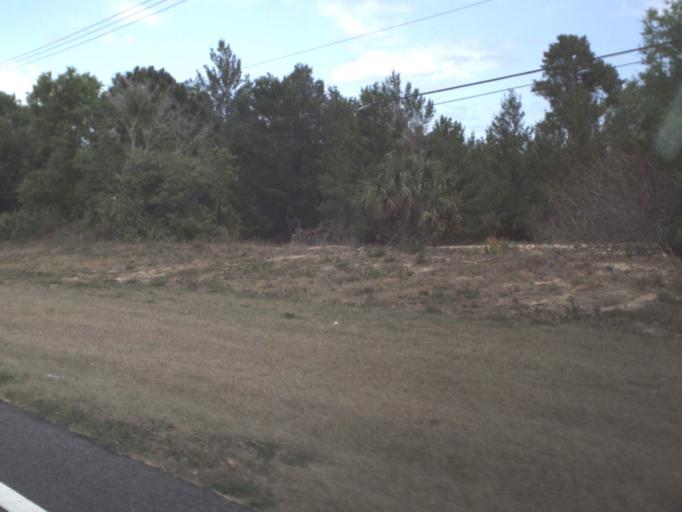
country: US
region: Florida
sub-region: Brevard County
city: Port Saint John
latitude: 28.5308
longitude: -80.8121
